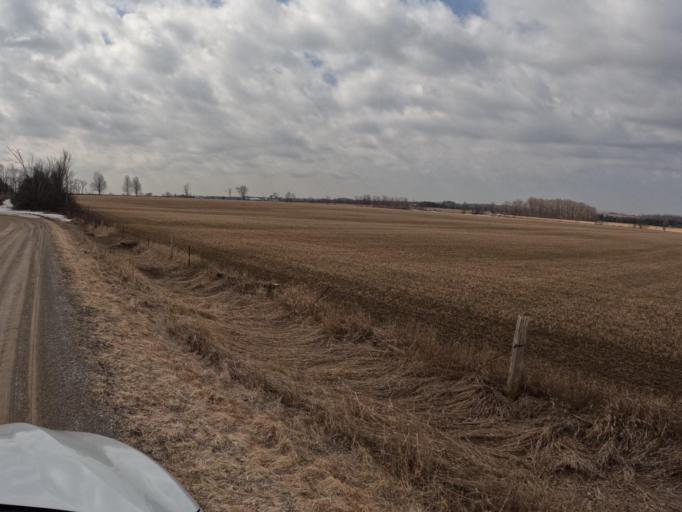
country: CA
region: Ontario
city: Shelburne
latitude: 43.9430
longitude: -80.2469
